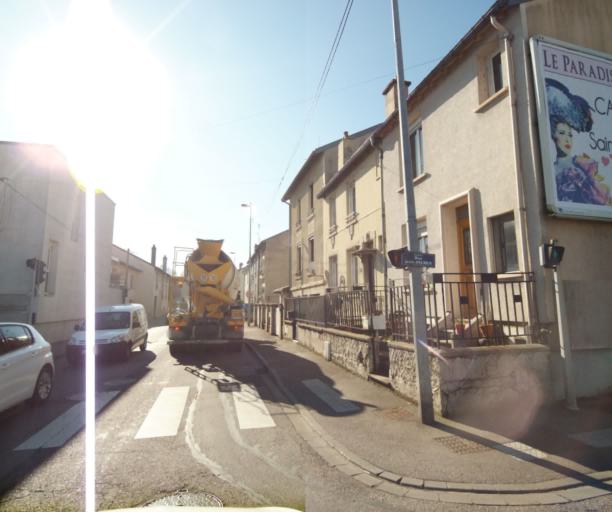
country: FR
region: Lorraine
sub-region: Departement de Meurthe-et-Moselle
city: Maxeville
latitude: 48.7085
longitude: 6.1718
